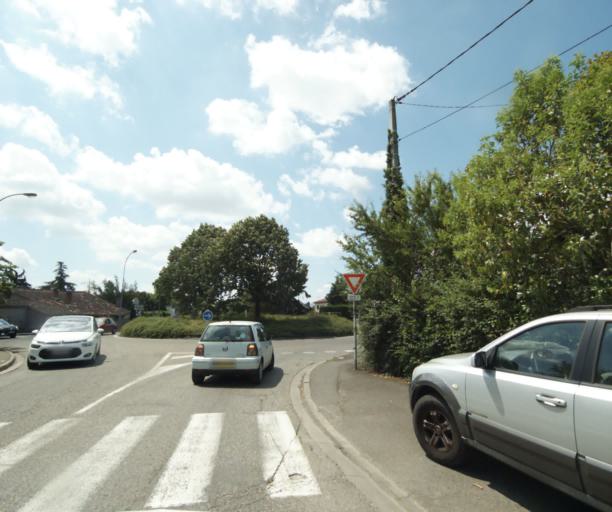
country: FR
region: Midi-Pyrenees
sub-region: Departement du Tarn-et-Garonne
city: Montauban
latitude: 44.0349
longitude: 1.3573
